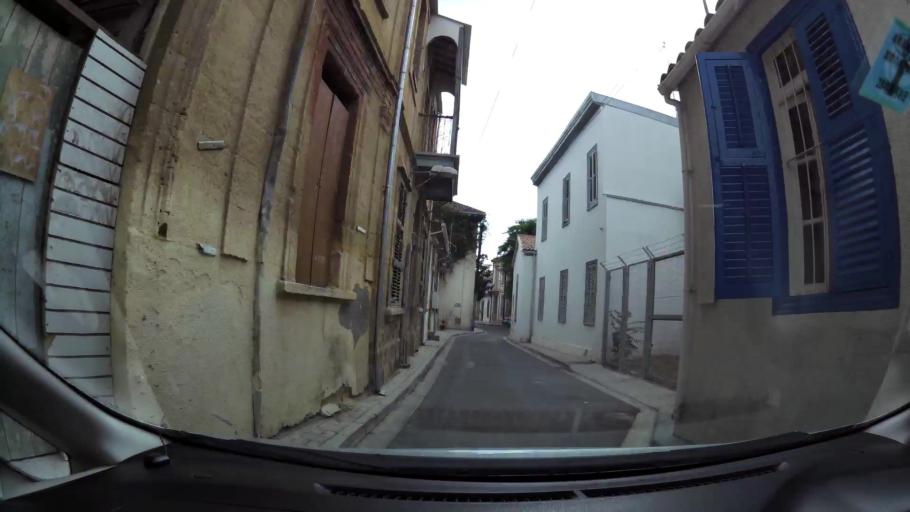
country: CY
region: Lefkosia
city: Nicosia
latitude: 35.1736
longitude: 33.3703
